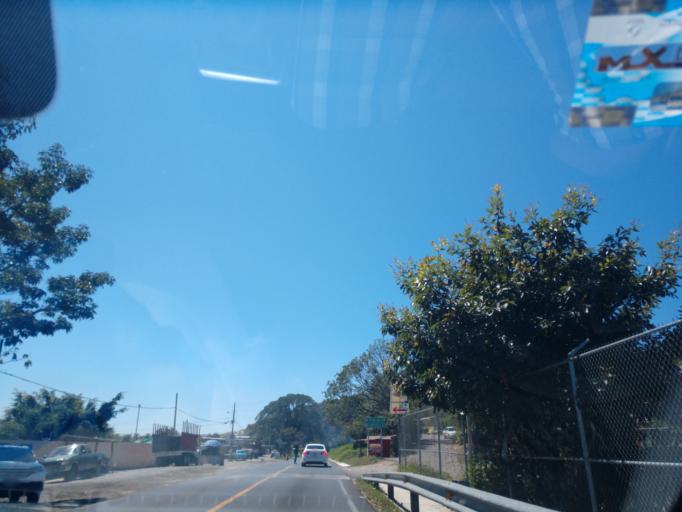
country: MX
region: Nayarit
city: Xalisco
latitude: 21.4004
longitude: -104.8951
